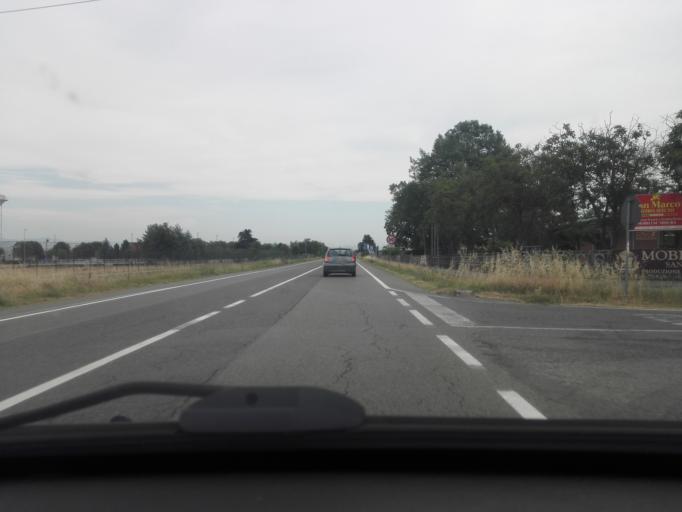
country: IT
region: Piedmont
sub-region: Provincia di Alessandria
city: Mandrogne
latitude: 44.8309
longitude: 8.7410
